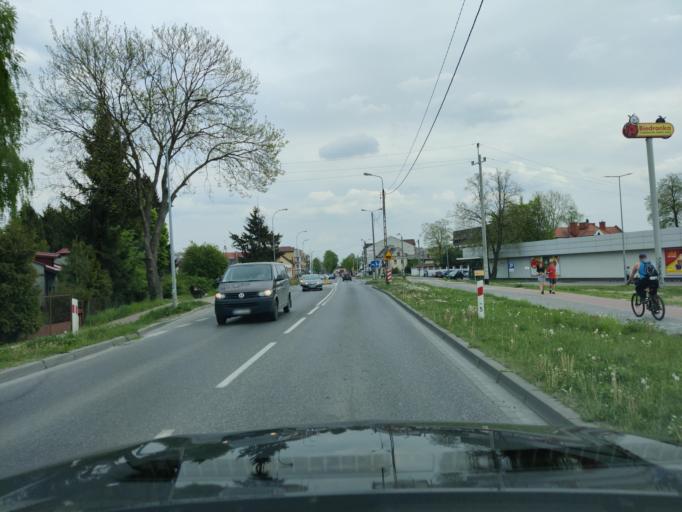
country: PL
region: Masovian Voivodeship
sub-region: Powiat wyszkowski
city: Wyszkow
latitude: 52.5983
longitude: 21.4433
